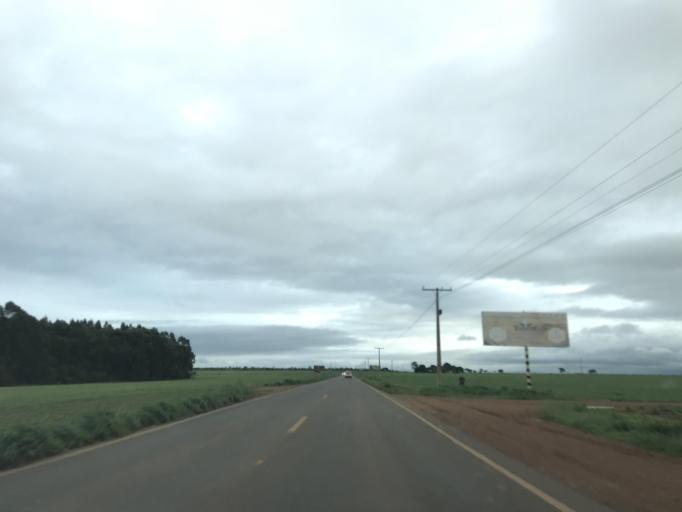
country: BR
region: Goias
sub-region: Luziania
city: Luziania
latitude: -16.3048
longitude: -48.0118
